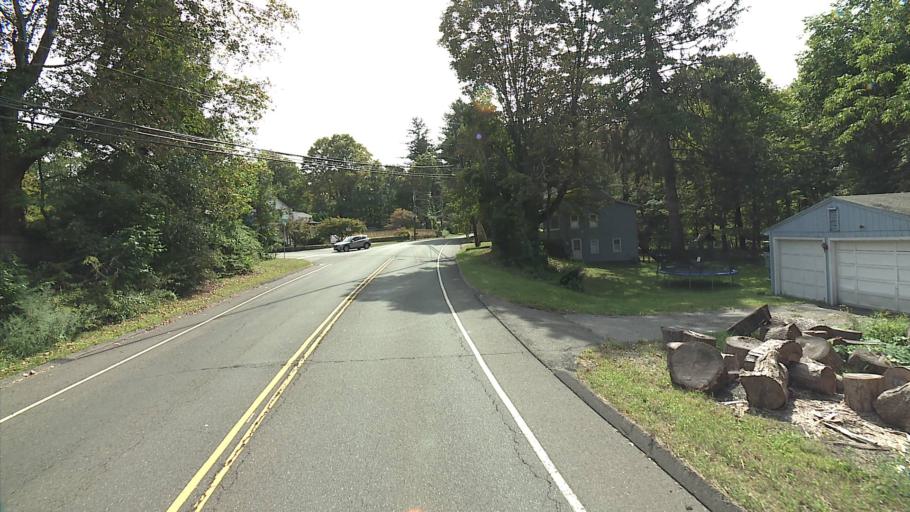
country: US
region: Connecticut
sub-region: Fairfield County
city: North Stamford
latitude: 41.1713
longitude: -73.5634
